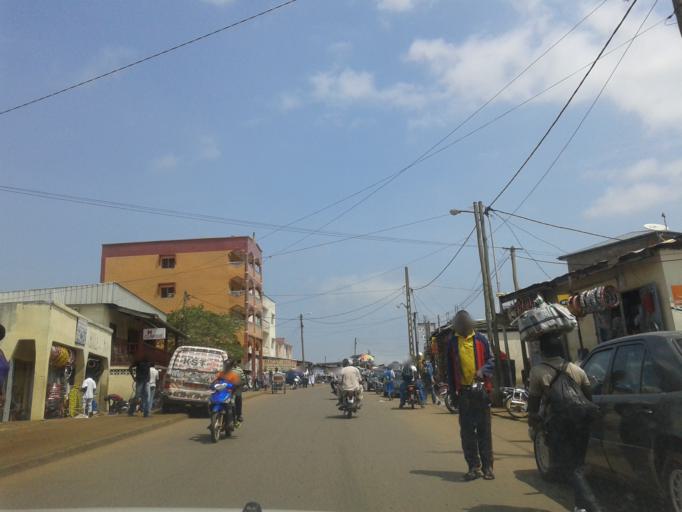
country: CM
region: Centre
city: Yaounde
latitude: 3.8757
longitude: 11.5112
